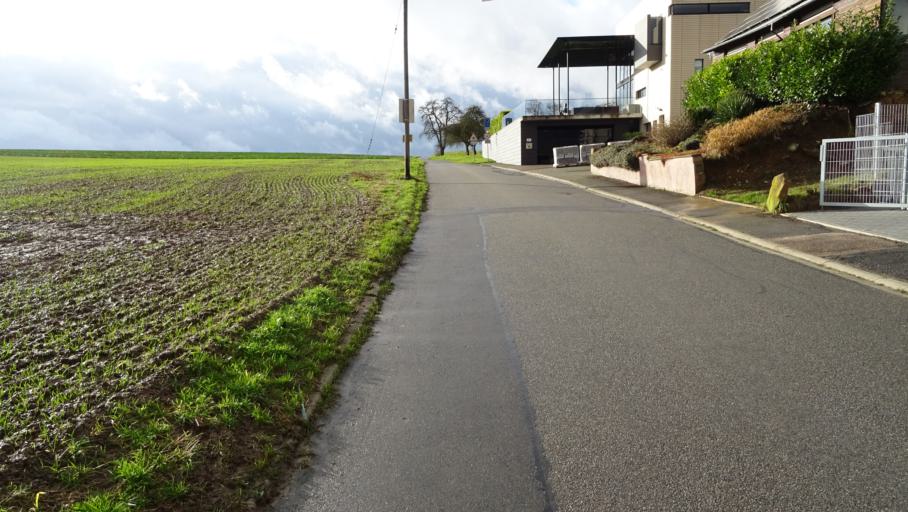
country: DE
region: Baden-Wuerttemberg
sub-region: Karlsruhe Region
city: Seckach
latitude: 49.4432
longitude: 9.2832
